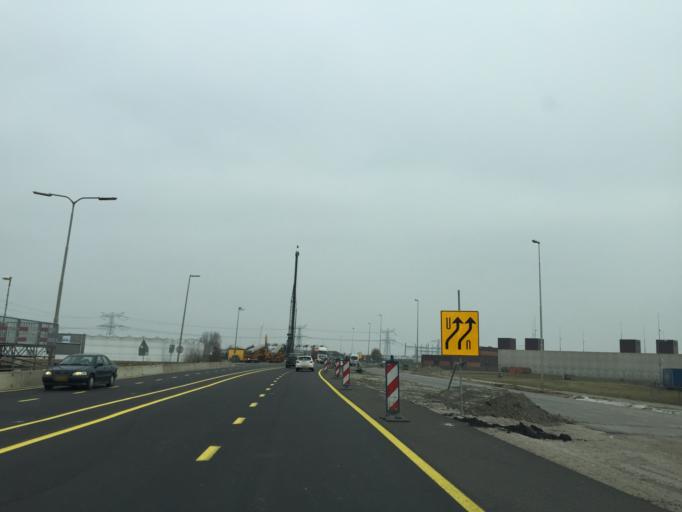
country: NL
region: South Holland
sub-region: Gemeente Westland
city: Maasdijk
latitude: 51.9751
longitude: 4.2173
